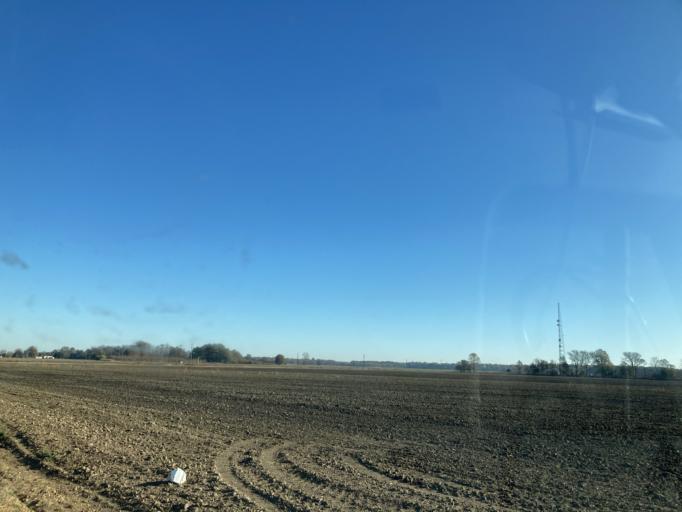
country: US
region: Mississippi
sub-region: Yazoo County
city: Yazoo City
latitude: 32.9208
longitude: -90.5942
